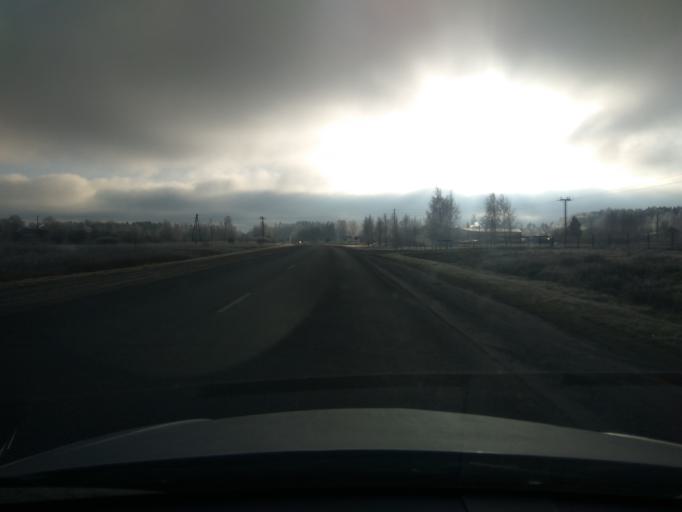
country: LV
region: Kuldigas Rajons
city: Kuldiga
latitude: 56.9684
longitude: 21.9338
